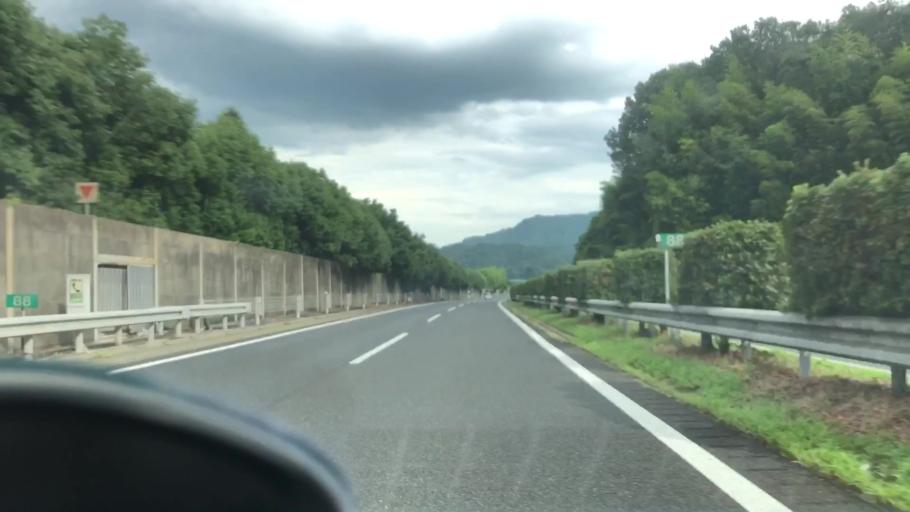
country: JP
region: Hyogo
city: Yamazakicho-nakabirose
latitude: 34.9688
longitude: 134.6725
